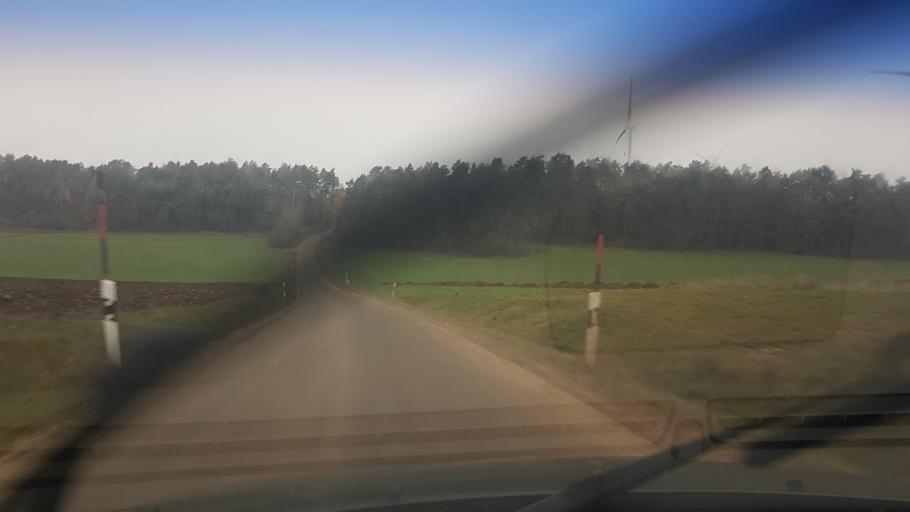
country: DE
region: Bavaria
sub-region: Upper Franconia
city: Kasendorf
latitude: 50.0387
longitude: 11.2919
